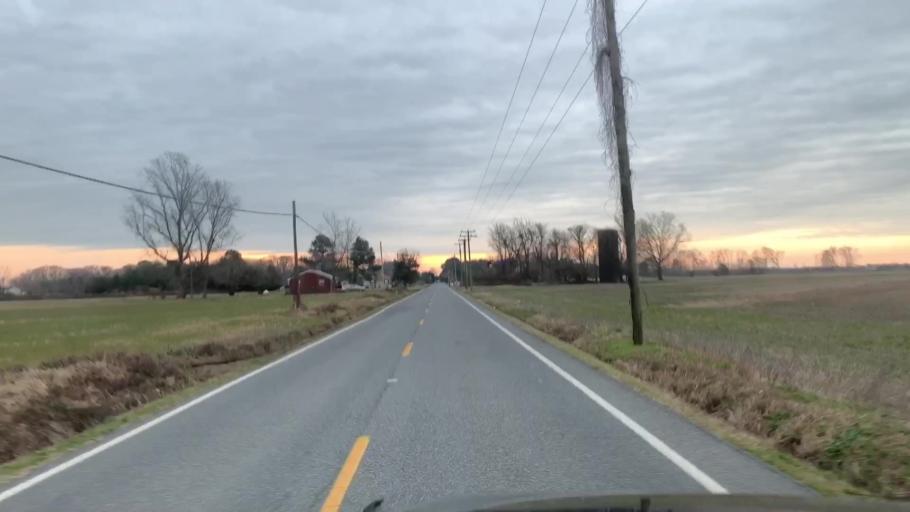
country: US
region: North Carolina
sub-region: Currituck County
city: Moyock
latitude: 36.6273
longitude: -76.1670
